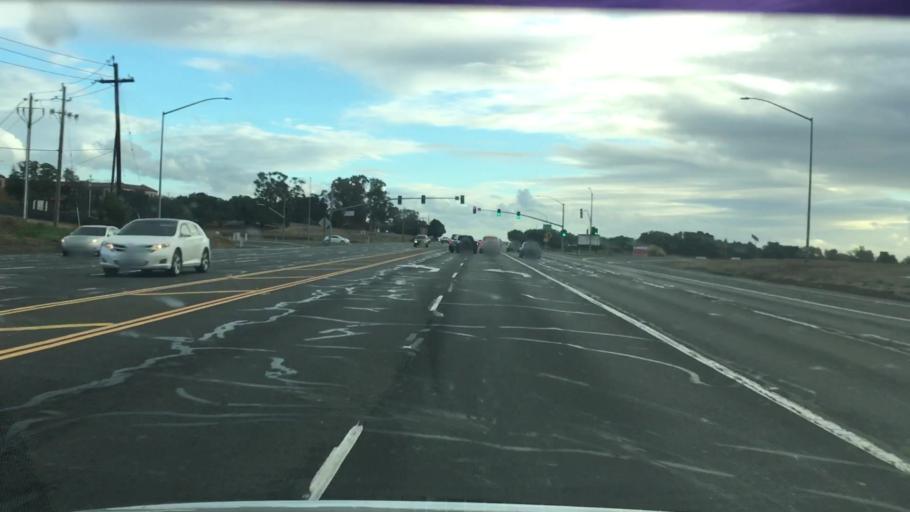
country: US
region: California
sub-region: Napa County
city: American Canyon
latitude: 38.2245
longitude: -122.2581
